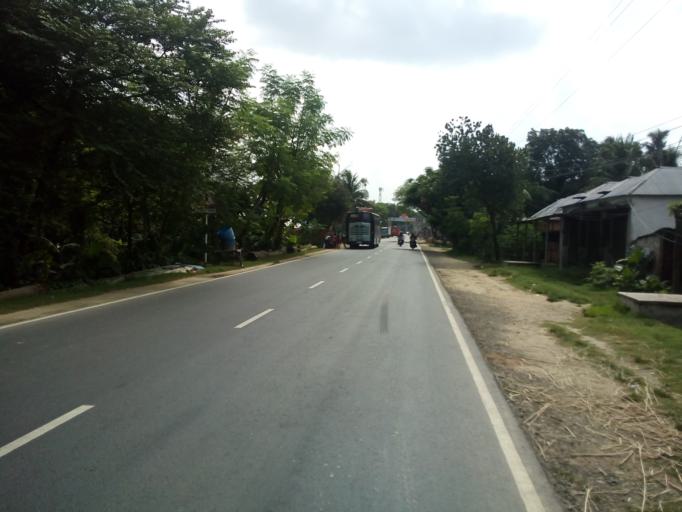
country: BD
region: Khulna
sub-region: Magura
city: Magura
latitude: 23.5279
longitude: 89.5877
